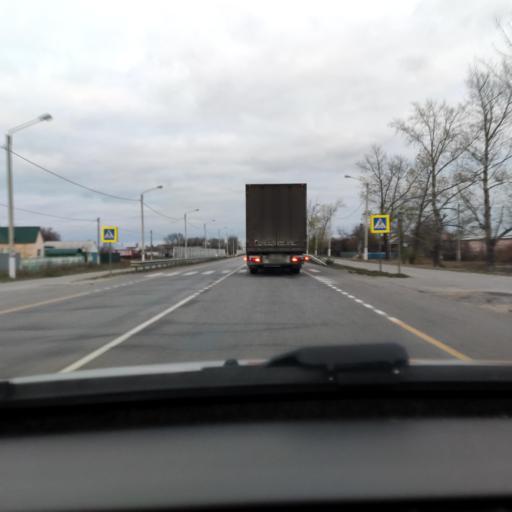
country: RU
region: Lipetsk
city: Khlevnoye
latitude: 52.2646
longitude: 39.1625
